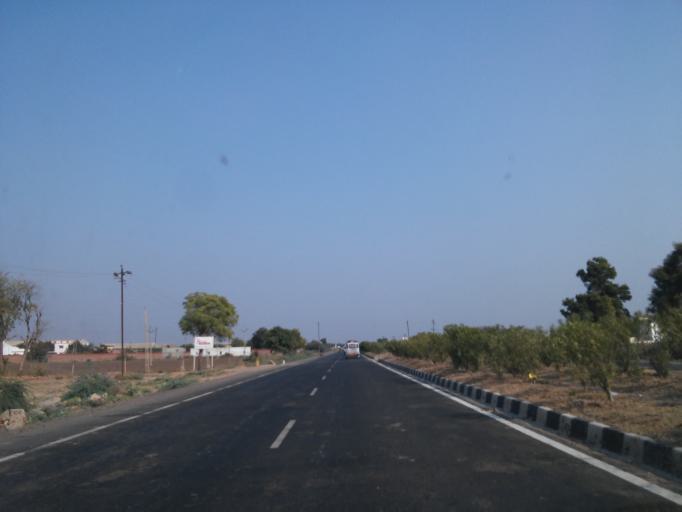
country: IN
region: Gujarat
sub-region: Surendranagar
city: Halvad
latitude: 23.0046
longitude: 71.1552
